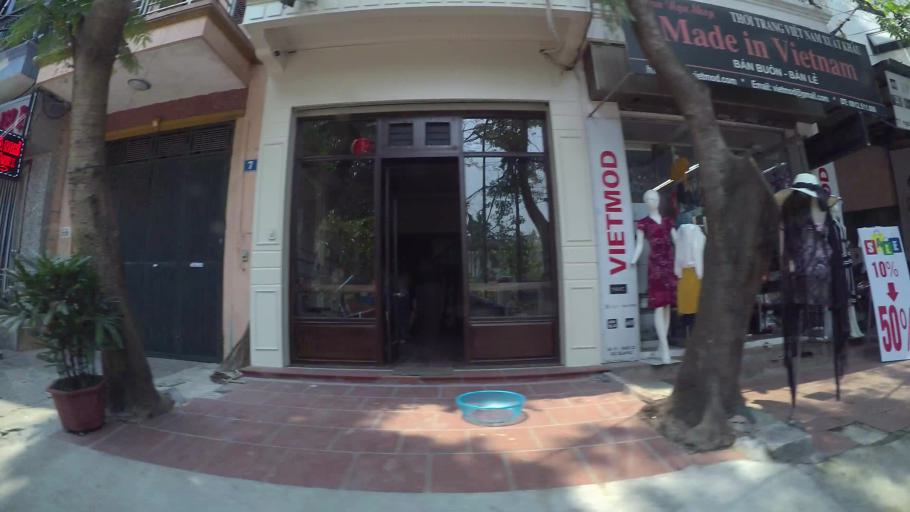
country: VN
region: Ha Noi
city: Thanh Xuan
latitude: 21.0116
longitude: 105.8022
